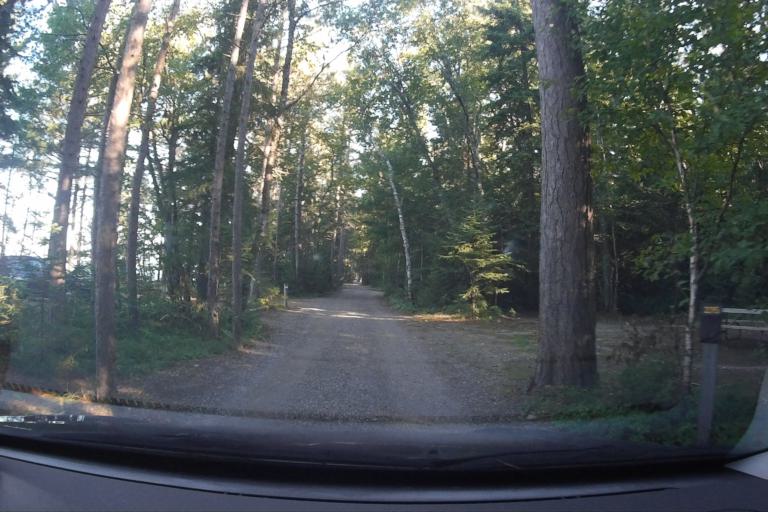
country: CA
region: Ontario
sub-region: Algoma
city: Sault Ste. Marie
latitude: 47.3241
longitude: -84.6106
